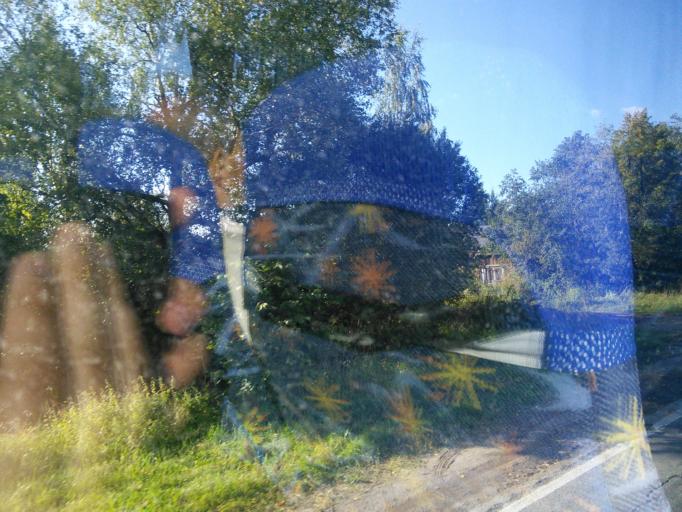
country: RU
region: Jaroslavl
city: Rybinsk
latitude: 58.2780
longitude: 38.8604
